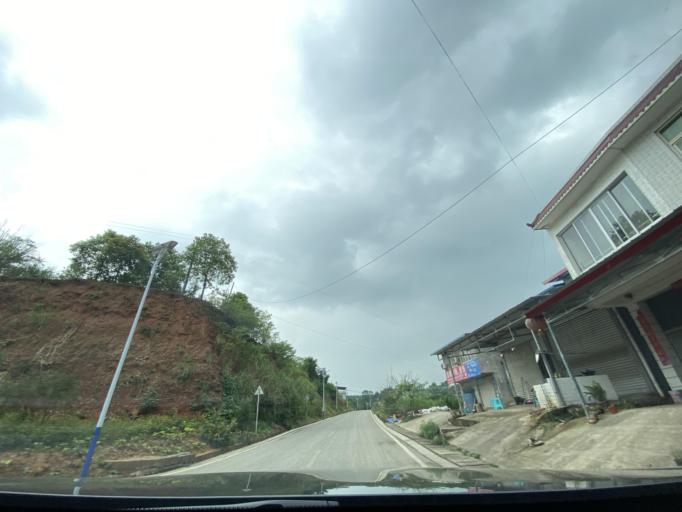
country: CN
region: Sichuan
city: Jiancheng
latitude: 30.5439
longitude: 104.5194
